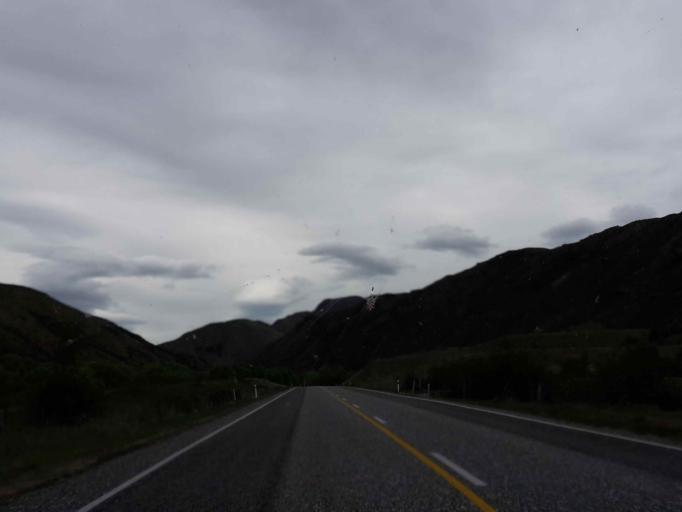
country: NZ
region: Otago
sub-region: Queenstown-Lakes District
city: Wanaka
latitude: -44.6342
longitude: 169.5129
